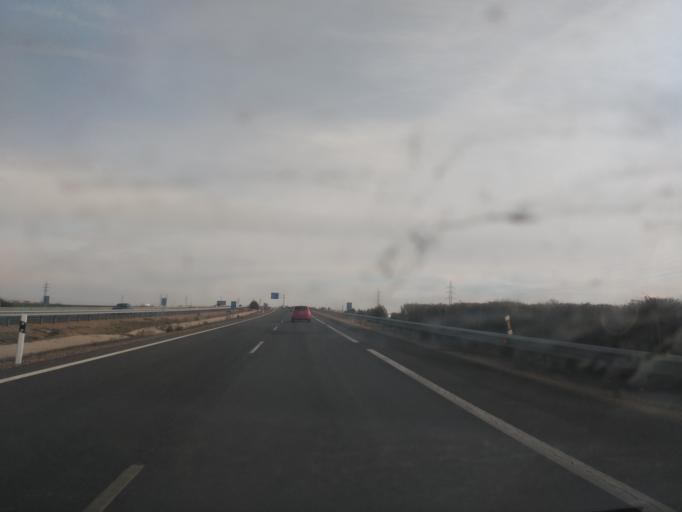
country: ES
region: Castille and Leon
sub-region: Provincia de Salamanca
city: Villares de la Reina
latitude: 41.0000
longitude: -5.6442
